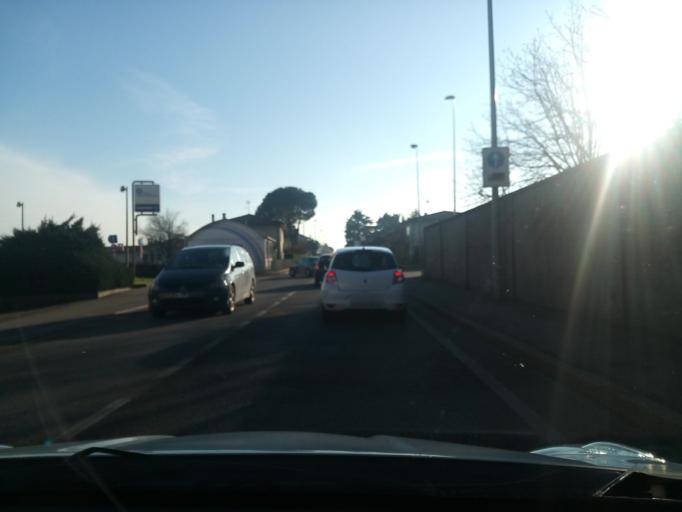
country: IT
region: Veneto
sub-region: Provincia di Vicenza
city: Villaverla
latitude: 45.6495
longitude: 11.4936
